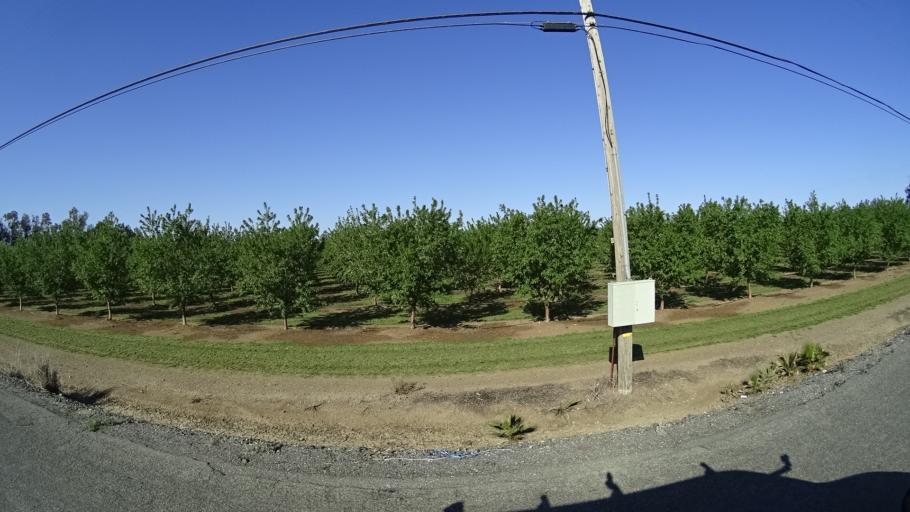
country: US
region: California
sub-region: Glenn County
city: Orland
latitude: 39.8108
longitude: -122.1040
